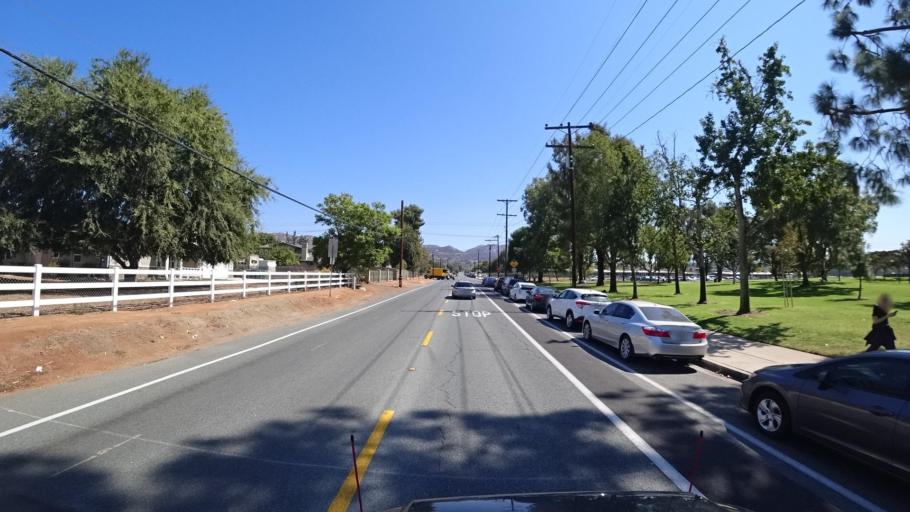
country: US
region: California
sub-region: San Diego County
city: Granite Hills
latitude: 32.8002
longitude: -116.9193
